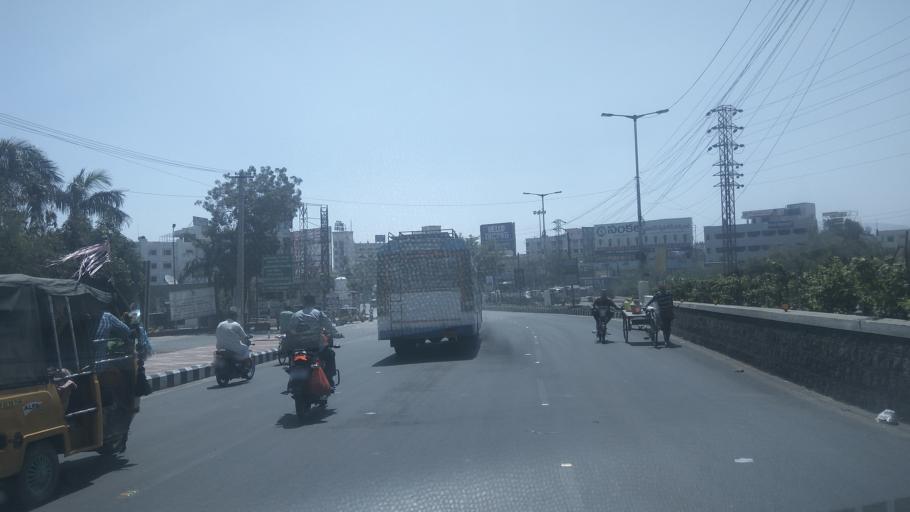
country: IN
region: Andhra Pradesh
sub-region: Chittoor
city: Tirupati
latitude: 13.6272
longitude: 79.4300
